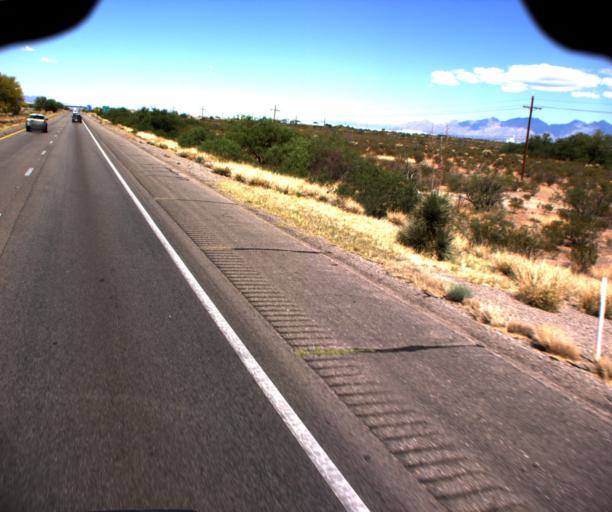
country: US
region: Arizona
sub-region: Pima County
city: Vail
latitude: 32.0778
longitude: -110.7992
